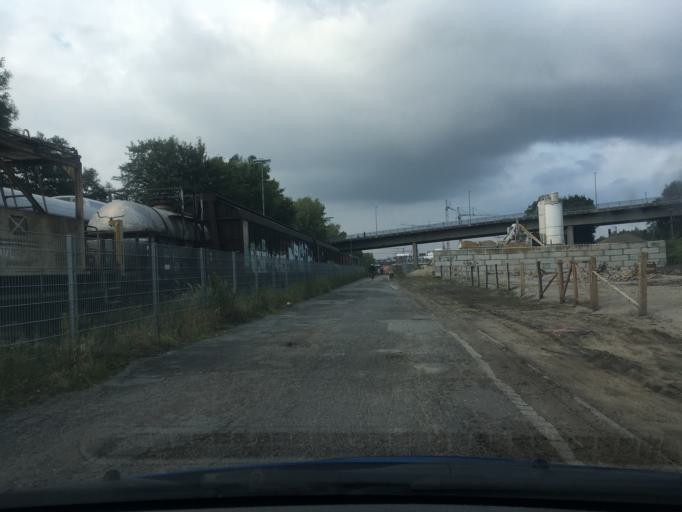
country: DE
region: Lower Saxony
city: Lueneburg
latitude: 53.2377
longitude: 10.4195
